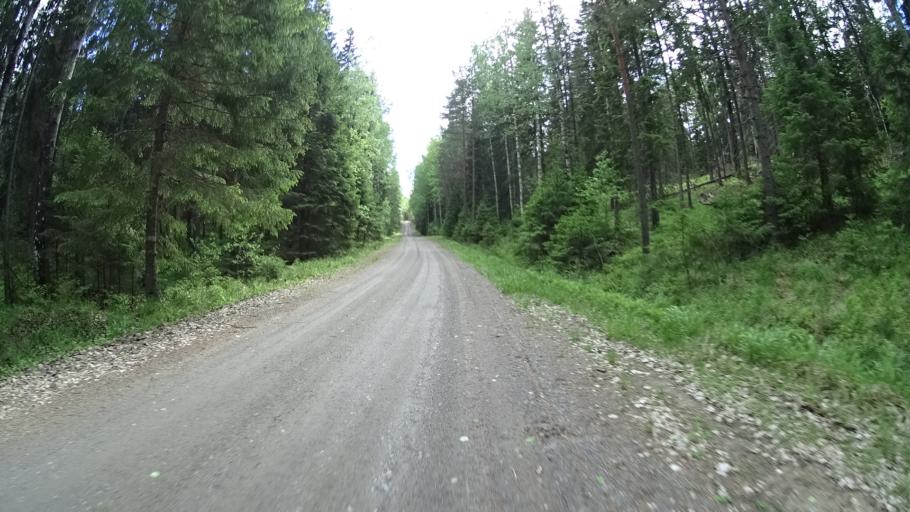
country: FI
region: Varsinais-Suomi
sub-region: Salo
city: Kisko
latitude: 60.1809
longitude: 23.5329
